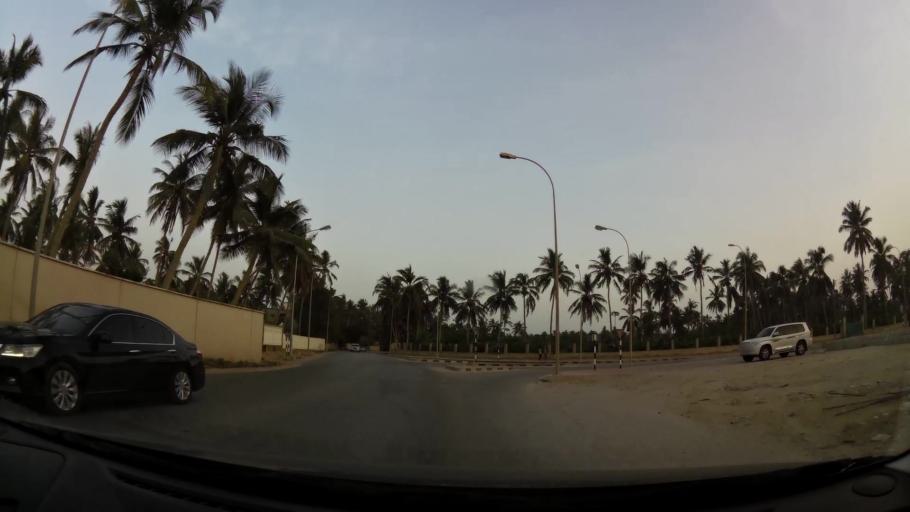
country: OM
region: Zufar
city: Salalah
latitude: 17.0195
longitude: 54.1291
